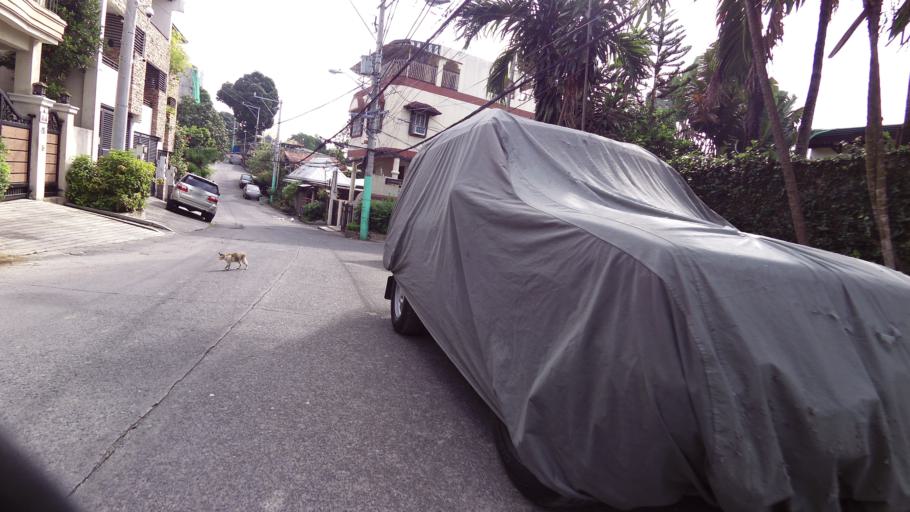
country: PH
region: Metro Manila
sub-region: Pasig
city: Pasig City
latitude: 14.5667
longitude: 121.0603
